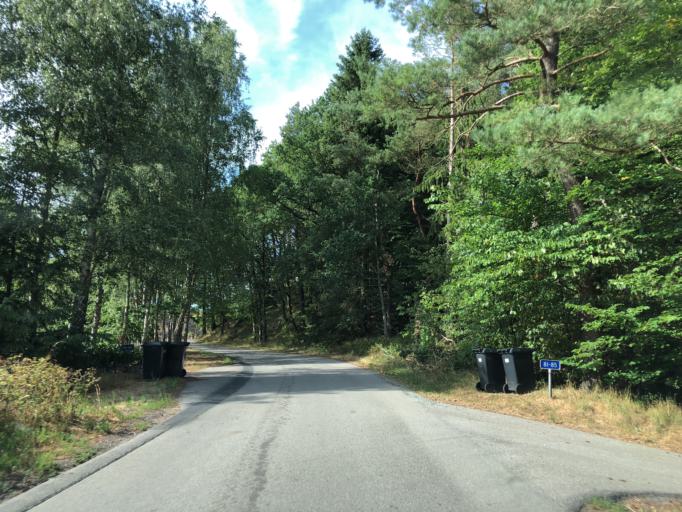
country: DK
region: South Denmark
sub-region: Vejle Kommune
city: Egtved
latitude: 55.6627
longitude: 9.3039
